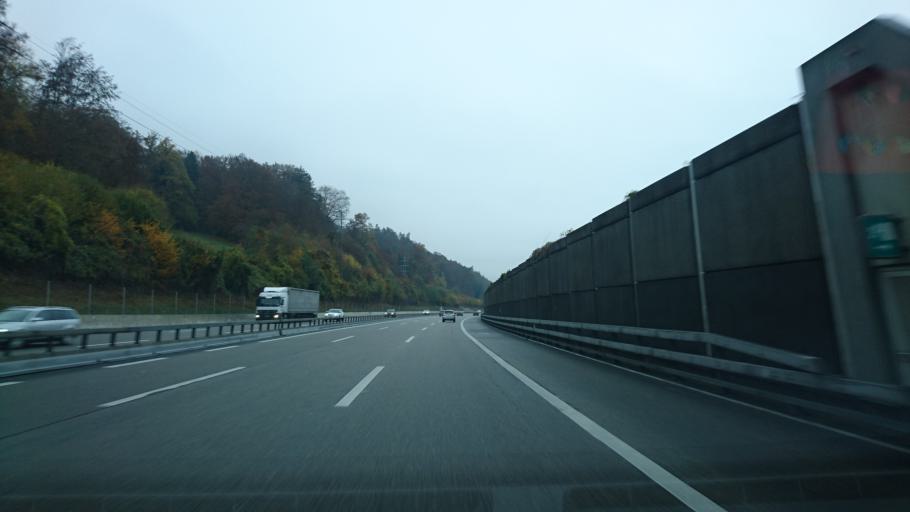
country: CH
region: Solothurn
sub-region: Bezirk Olten
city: Gunzgen
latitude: 47.3121
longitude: 7.8547
